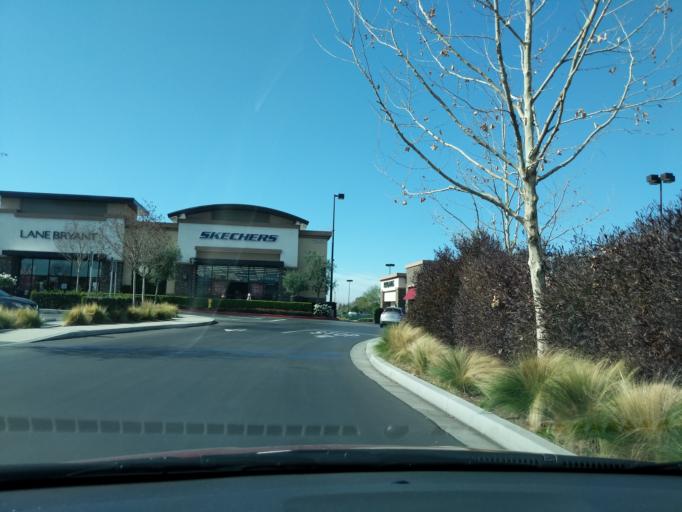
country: US
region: California
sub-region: San Bernardino County
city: Redlands
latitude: 34.0763
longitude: -117.2044
